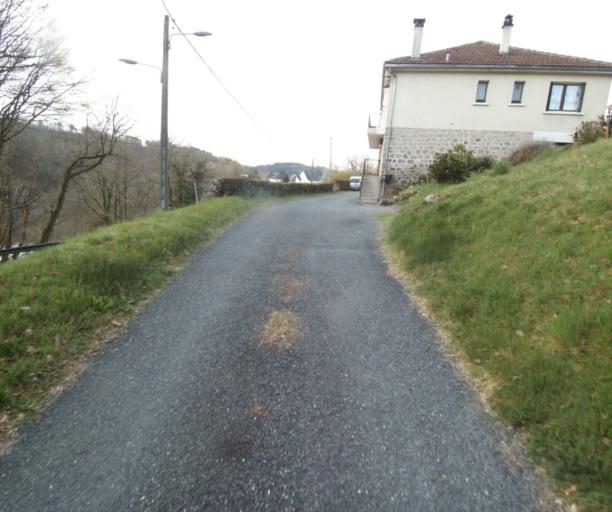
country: FR
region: Limousin
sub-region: Departement de la Correze
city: Correze
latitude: 45.3678
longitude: 1.8727
